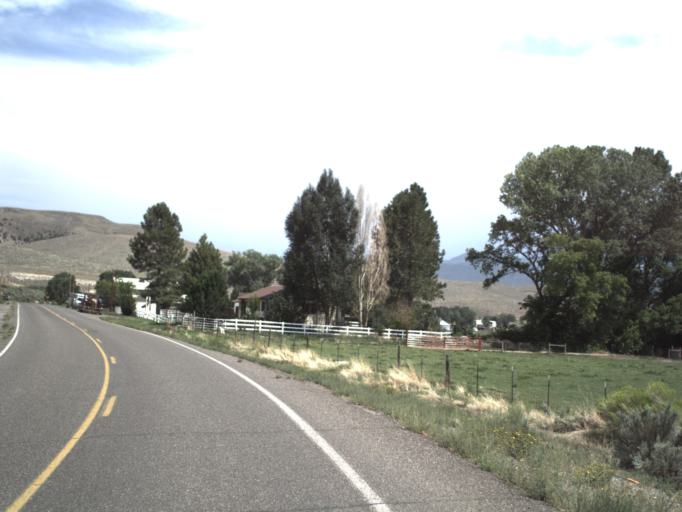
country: US
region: Utah
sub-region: Piute County
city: Junction
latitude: 38.1171
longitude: -112.0005
